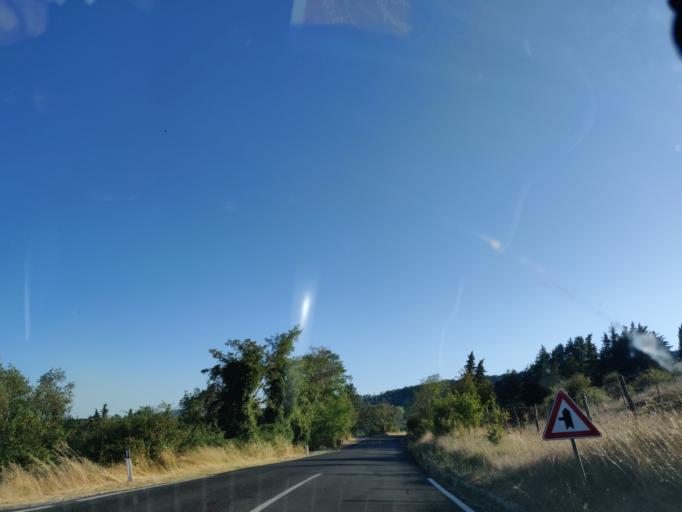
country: IT
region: Tuscany
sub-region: Provincia di Siena
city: Abbadia San Salvatore
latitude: 42.8707
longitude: 11.6846
